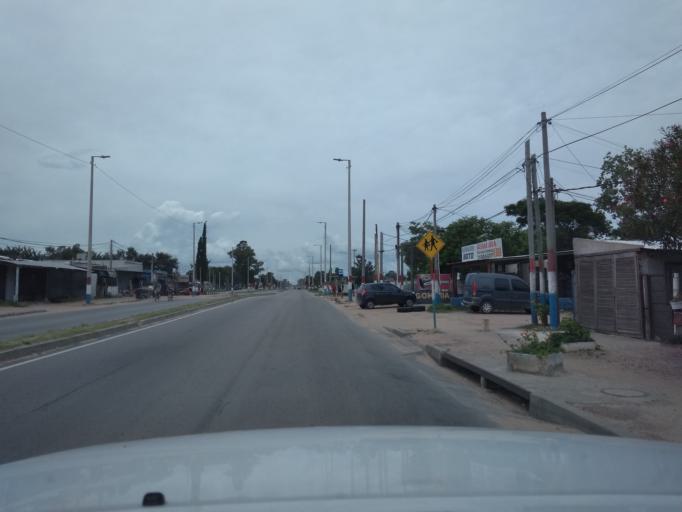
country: UY
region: Canelones
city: Paso de Carrasco
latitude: -34.8636
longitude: -56.0564
